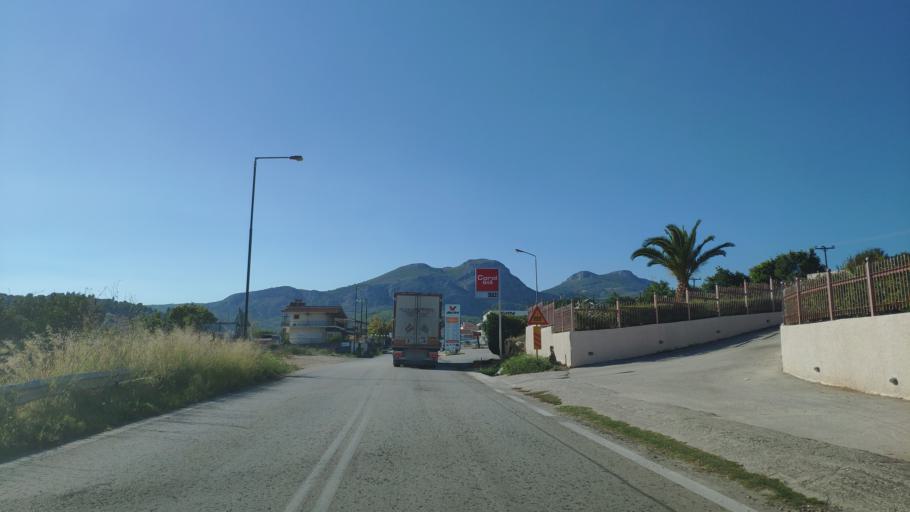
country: GR
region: Peloponnese
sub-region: Nomos Korinthias
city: Arkhaia Korinthos
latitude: 37.8830
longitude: 22.8919
